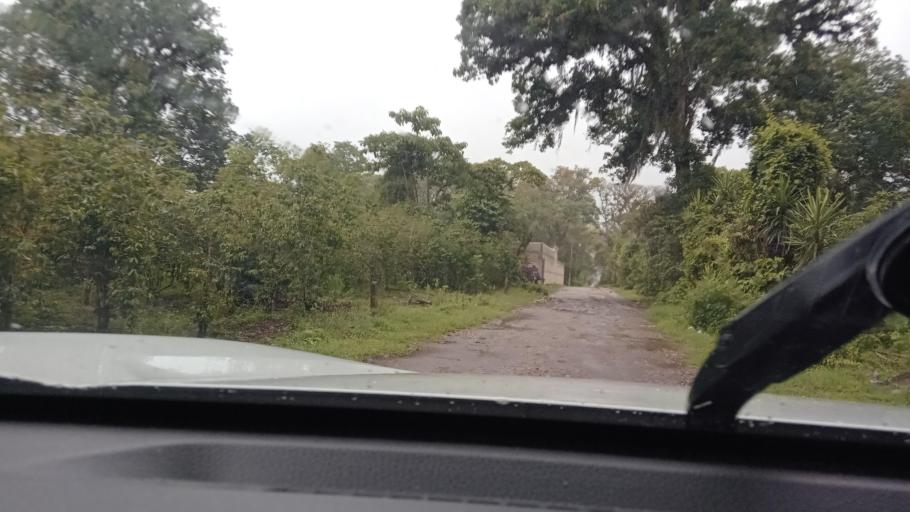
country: MX
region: Veracruz
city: Coatepec
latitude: 19.4546
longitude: -96.9767
